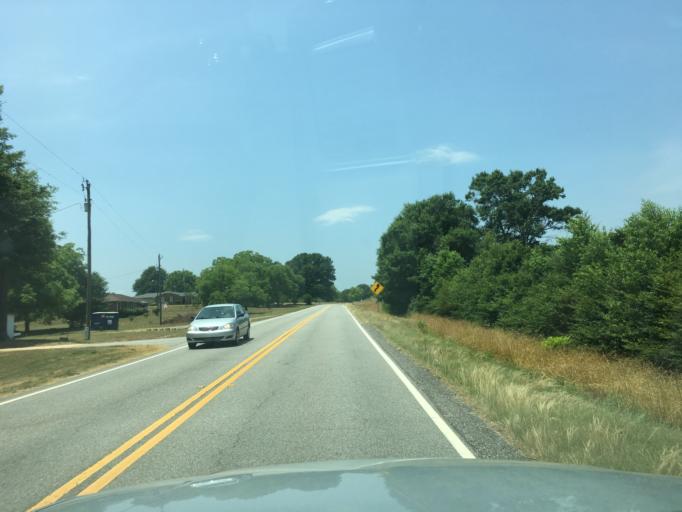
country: US
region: Georgia
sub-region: Hart County
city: Royston
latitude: 34.2289
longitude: -83.1929
